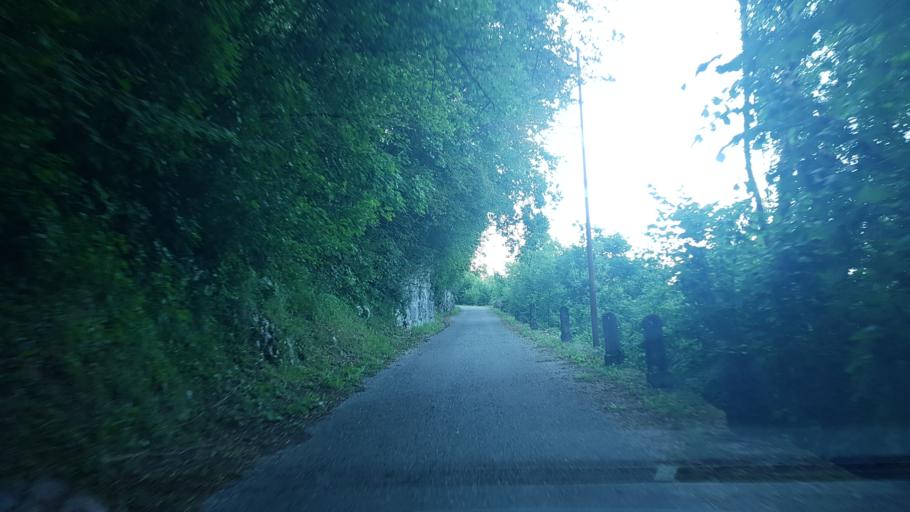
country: IT
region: Friuli Venezia Giulia
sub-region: Provincia di Udine
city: Nimis
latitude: 46.2335
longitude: 13.2503
